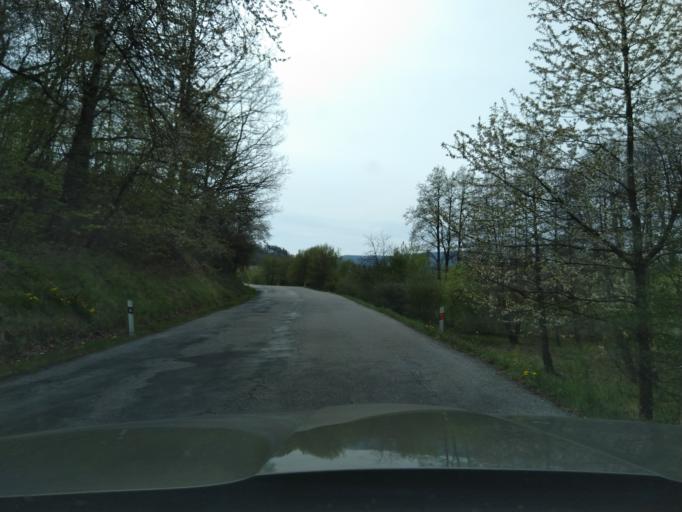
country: CZ
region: Plzensky
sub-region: Okres Klatovy
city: Susice
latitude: 49.2176
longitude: 13.6126
